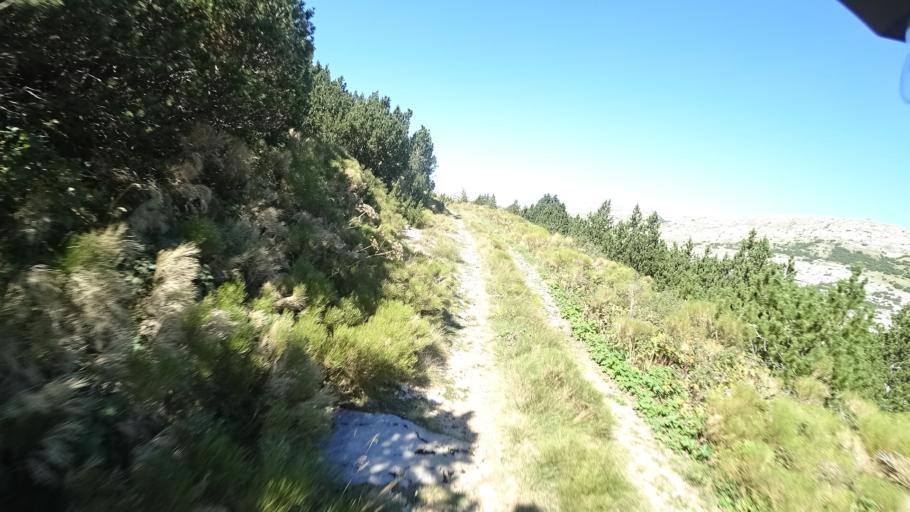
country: HR
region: Splitsko-Dalmatinska
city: Hrvace
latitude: 43.9418
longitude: 16.5746
